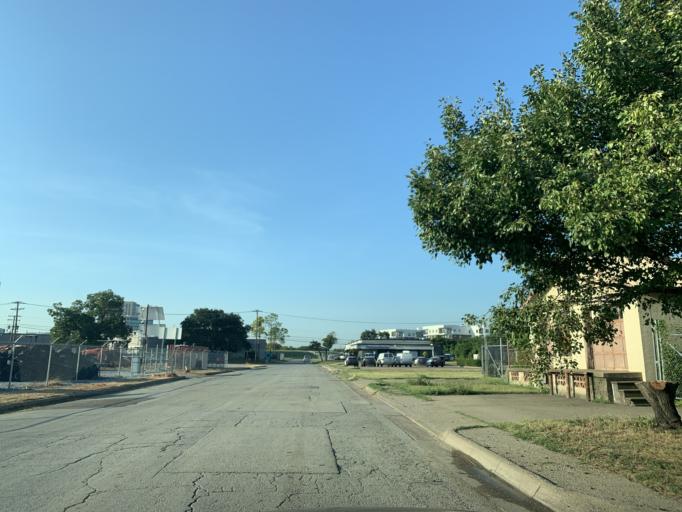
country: US
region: Texas
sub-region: Tarrant County
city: Fort Worth
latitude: 32.7579
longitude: -97.3469
